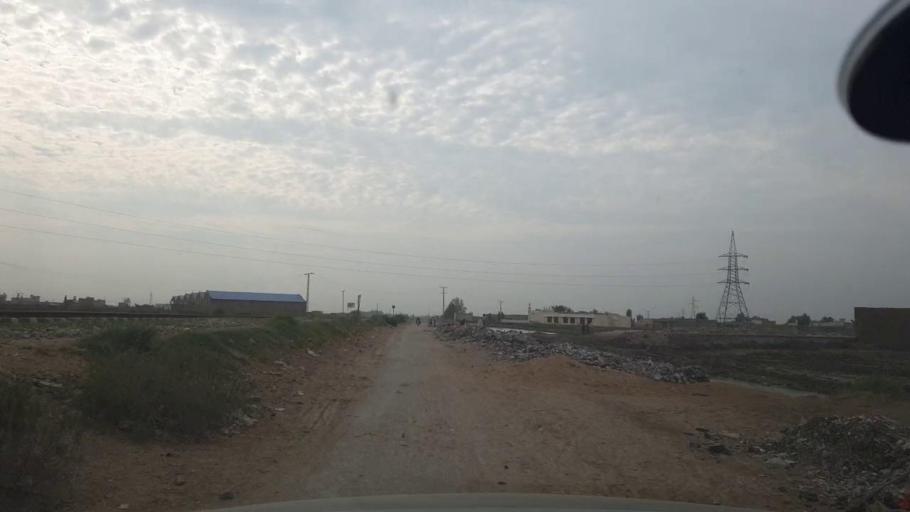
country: PK
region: Sindh
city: Jacobabad
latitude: 28.2609
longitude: 68.4496
